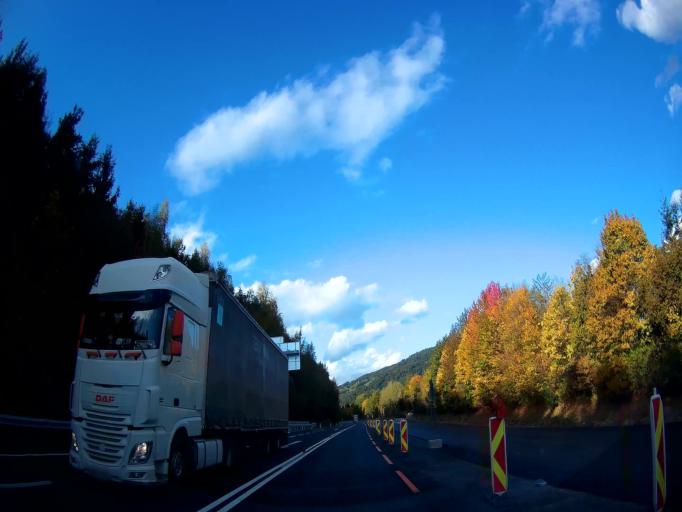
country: AT
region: Carinthia
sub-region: Politischer Bezirk Wolfsberg
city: Wolfsberg
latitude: 46.8520
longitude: 14.8353
